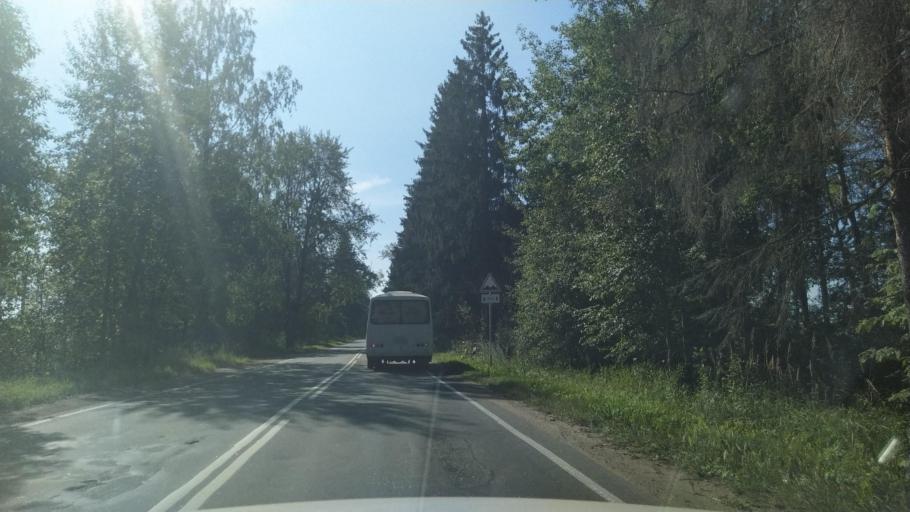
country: RU
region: Leningrad
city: Siverskiy
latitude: 59.3278
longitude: 30.0648
